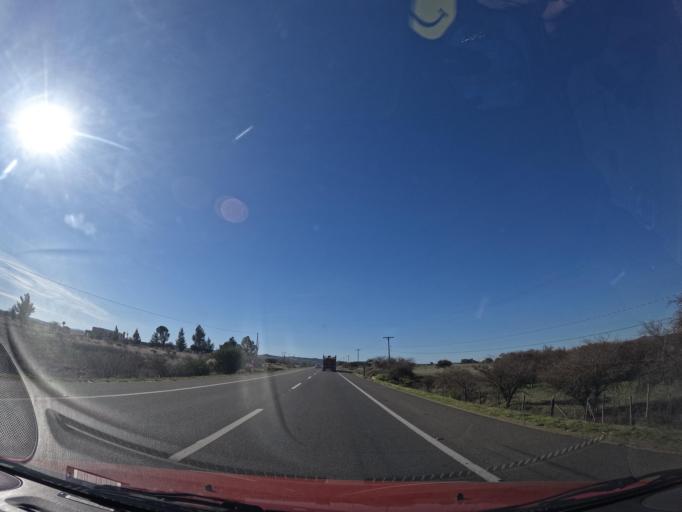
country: CL
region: Maule
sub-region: Provincia de Cauquenes
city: Cauquenes
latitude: -35.9571
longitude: -72.2139
